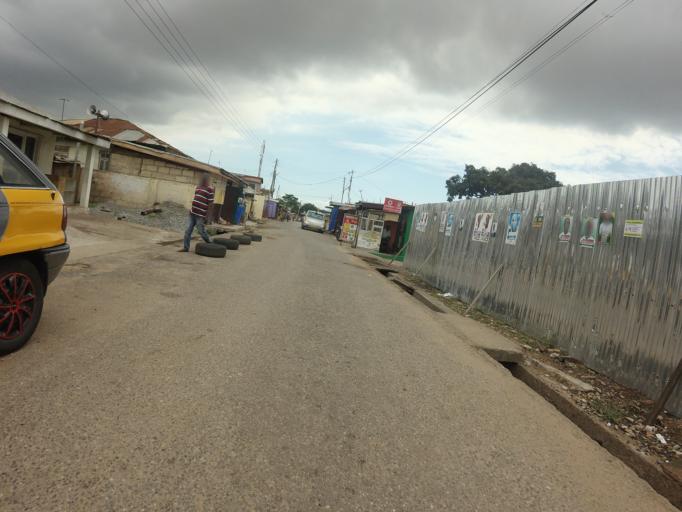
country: GH
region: Greater Accra
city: Accra
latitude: 5.5857
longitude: -0.2069
